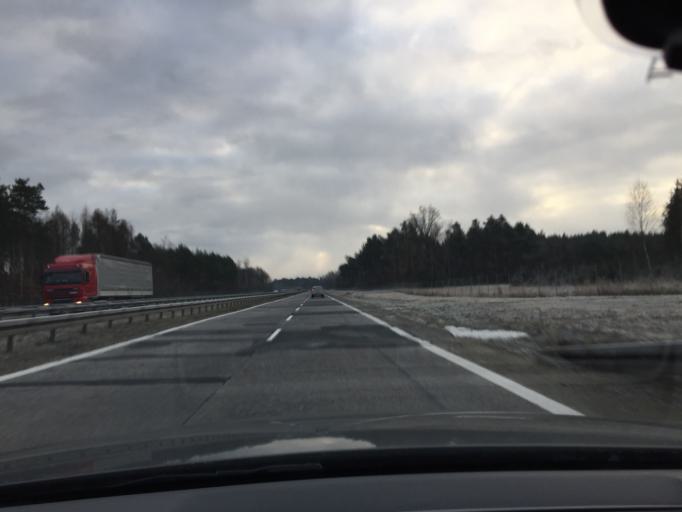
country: PL
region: Lubusz
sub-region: Powiat zarski
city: Lipinki Luzyckie
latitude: 51.6007
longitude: 14.9918
